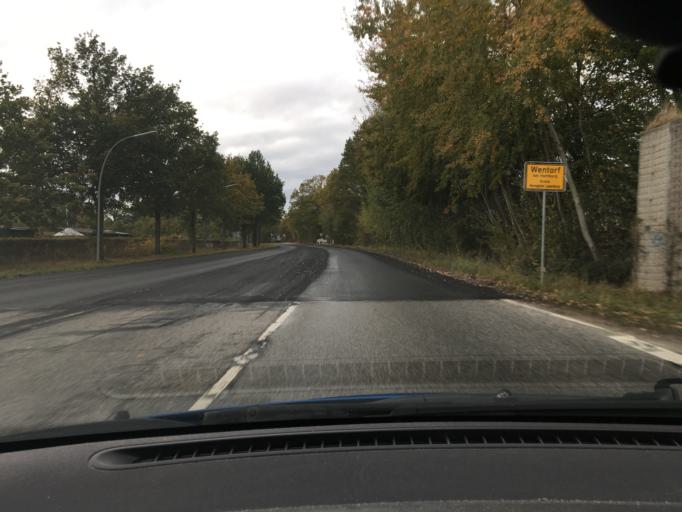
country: DE
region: Schleswig-Holstein
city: Bornsen
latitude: 53.4908
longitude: 10.2705
